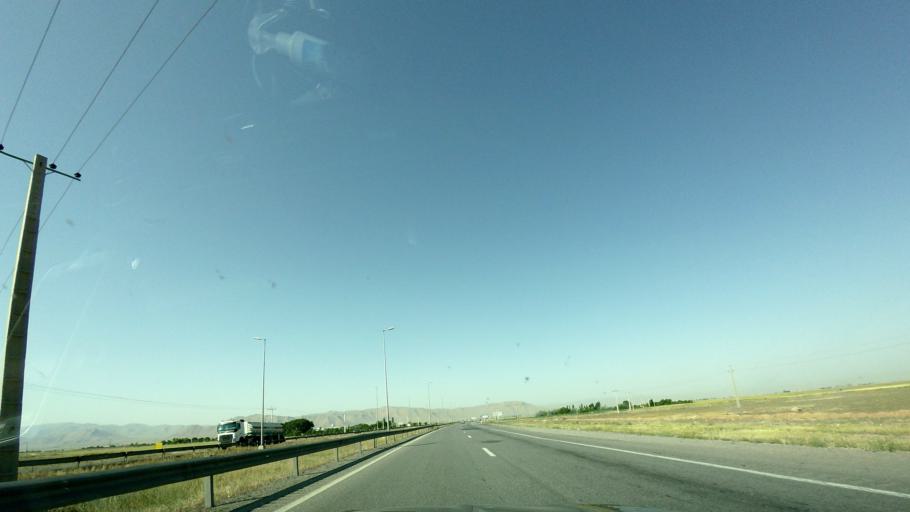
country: IR
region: Markazi
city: Ashtian
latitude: 34.1871
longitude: 50.0518
